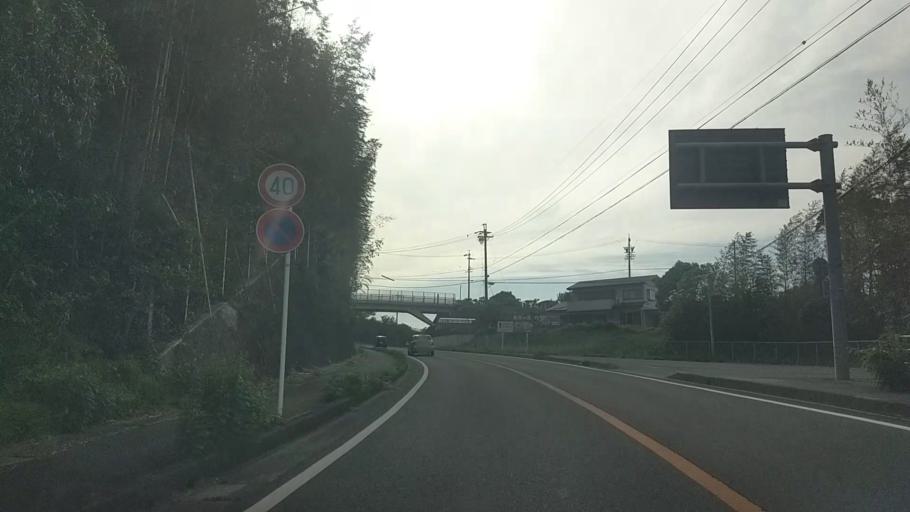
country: JP
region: Shizuoka
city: Hamamatsu
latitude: 34.7642
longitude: 137.6458
